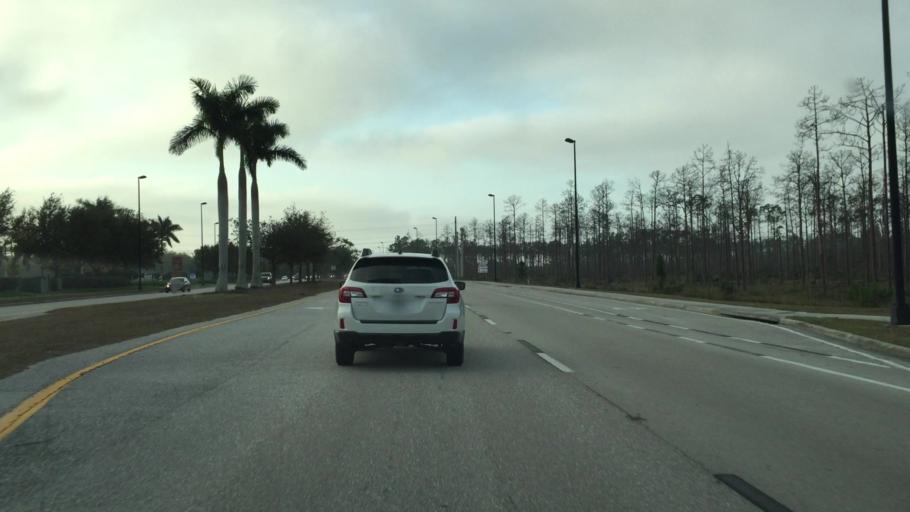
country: US
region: Florida
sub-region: Lee County
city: Three Oaks
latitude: 26.5032
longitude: -81.7853
